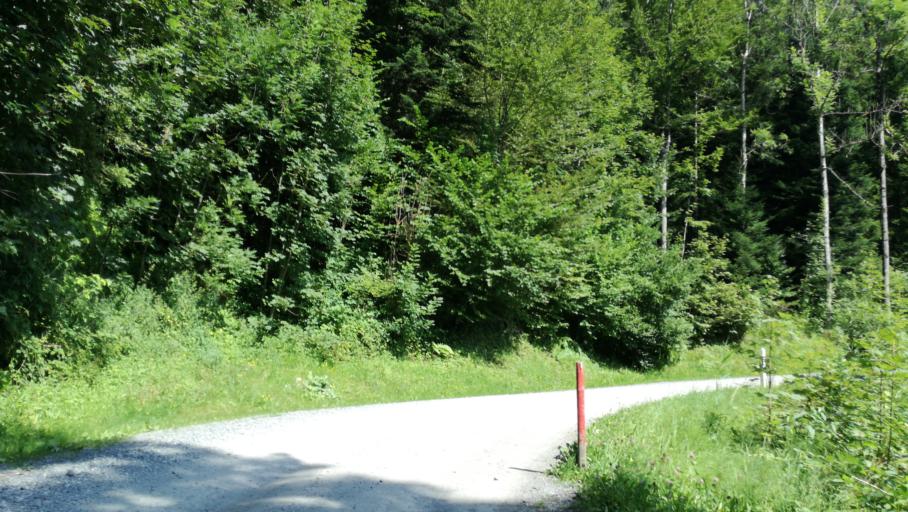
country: CH
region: Zug
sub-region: Zug
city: Unterageri
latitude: 47.1442
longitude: 8.5963
